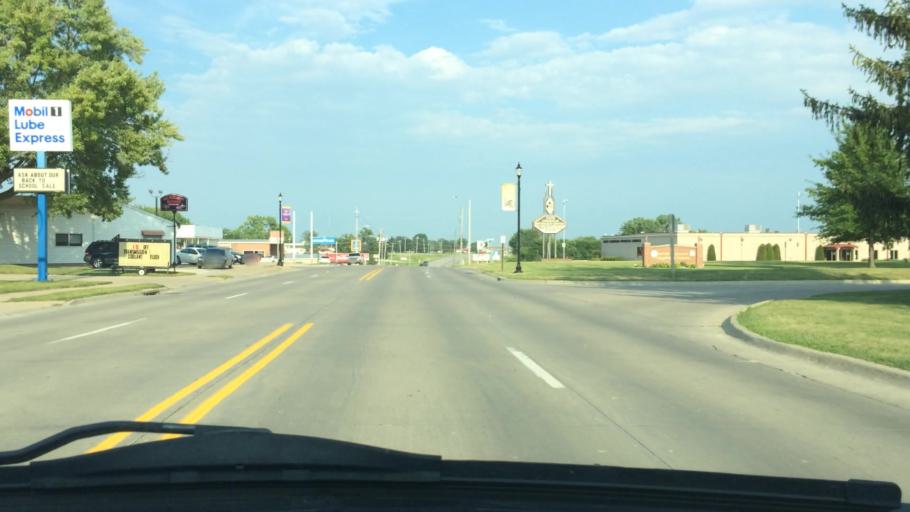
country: US
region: Iowa
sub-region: Henry County
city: Mount Pleasant
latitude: 40.9637
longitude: -91.5362
